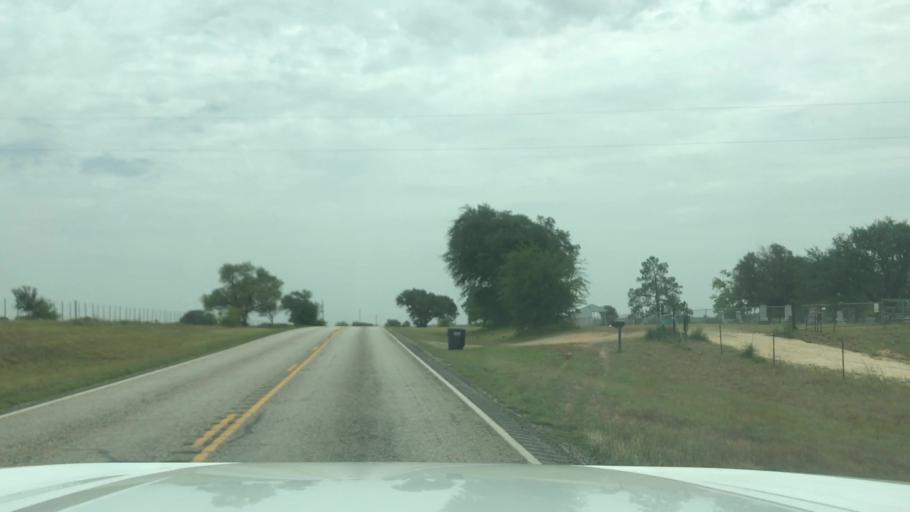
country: US
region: Texas
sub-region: Hamilton County
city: Hico
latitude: 32.0452
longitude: -98.1426
